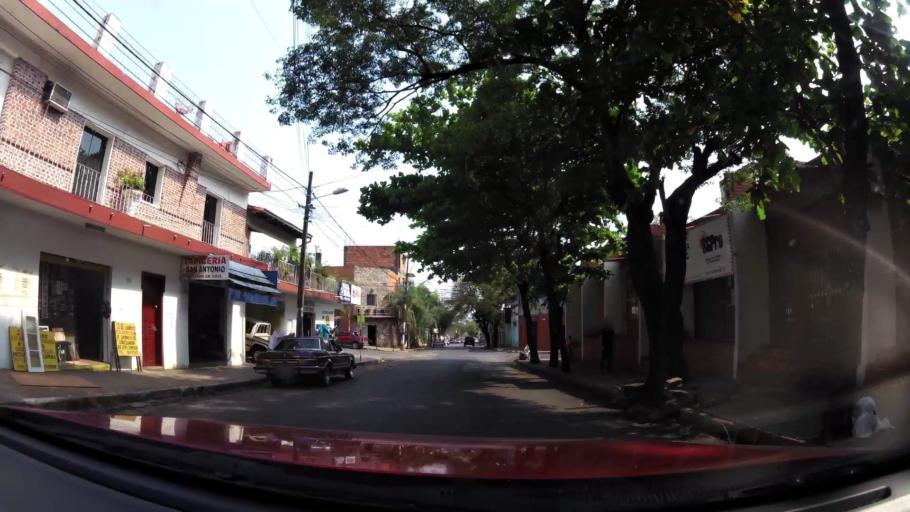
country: PY
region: Presidente Hayes
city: Nanawa
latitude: -25.2856
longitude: -57.6538
